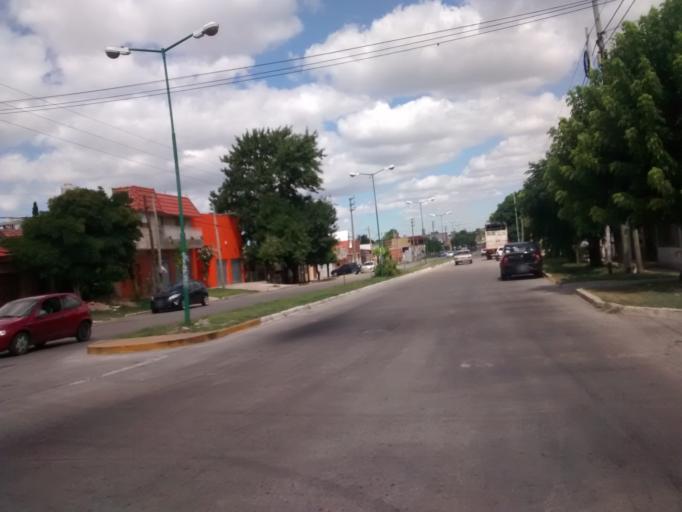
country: AR
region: Buenos Aires
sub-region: Partido de La Plata
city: La Plata
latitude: -34.9562
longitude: -57.9638
